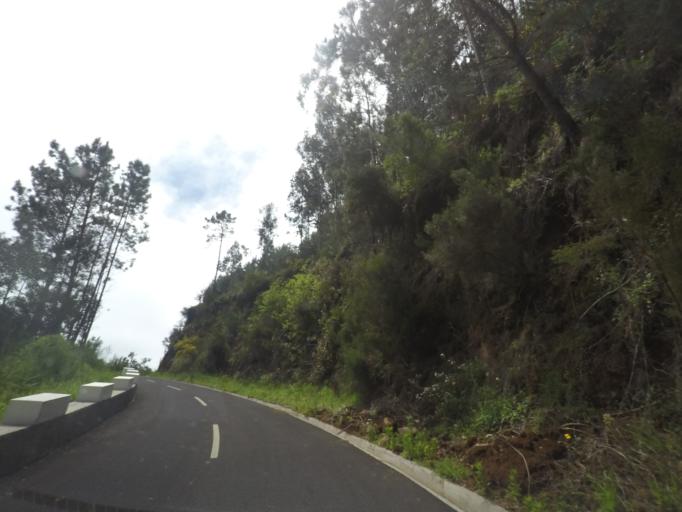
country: PT
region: Madeira
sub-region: Calheta
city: Arco da Calheta
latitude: 32.7251
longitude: -17.1180
